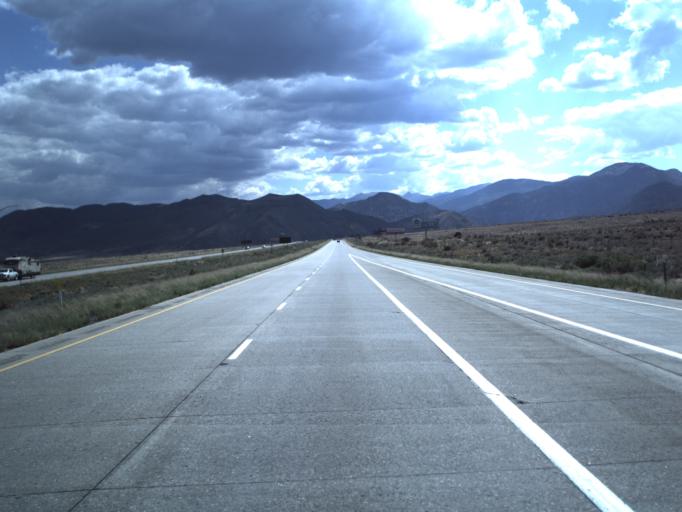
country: US
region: Utah
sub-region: Sevier County
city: Monroe
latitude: 38.6187
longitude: -112.2291
